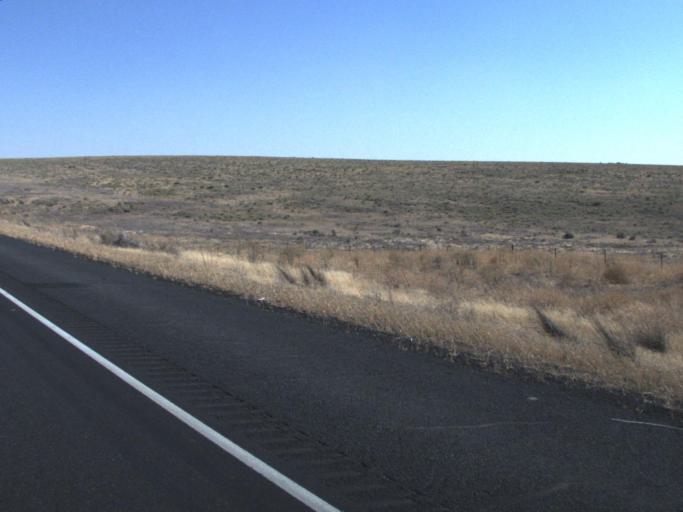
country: US
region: Washington
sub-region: Grant County
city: Warden
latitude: 47.0860
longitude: -118.7582
